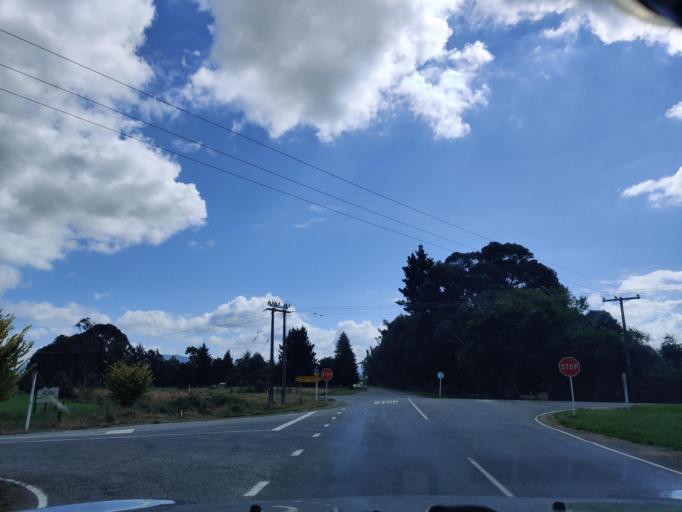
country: NZ
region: Canterbury
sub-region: Timaru District
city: Pleasant Point
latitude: -44.1127
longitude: 171.2245
